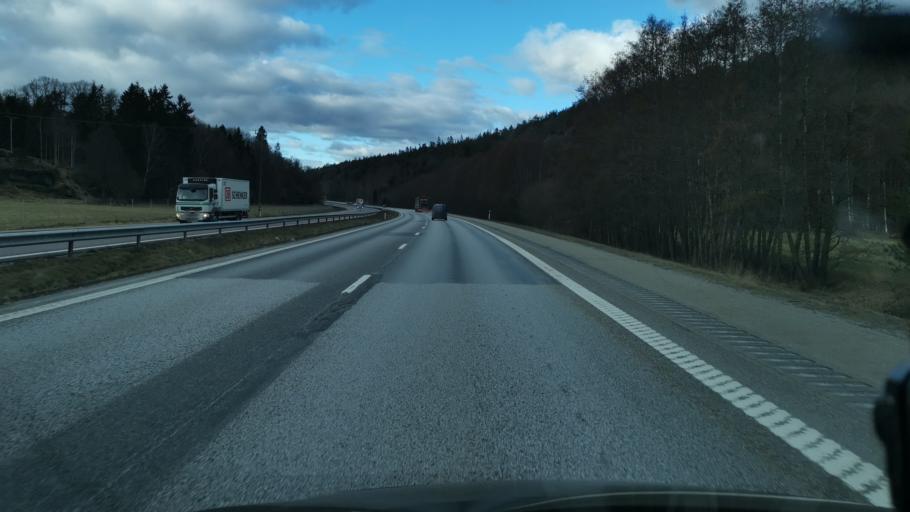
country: SE
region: Vaestra Goetaland
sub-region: Stenungsunds Kommun
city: Stenungsund
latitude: 58.0698
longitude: 11.8909
